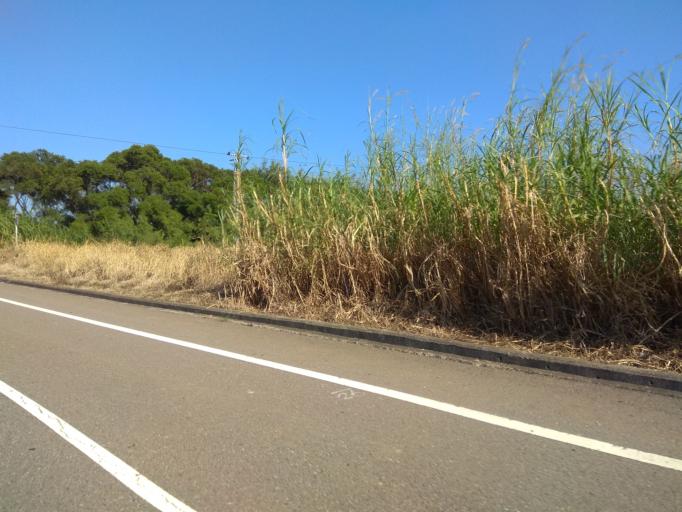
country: TW
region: Taiwan
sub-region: Hsinchu
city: Zhubei
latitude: 24.9934
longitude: 121.0345
